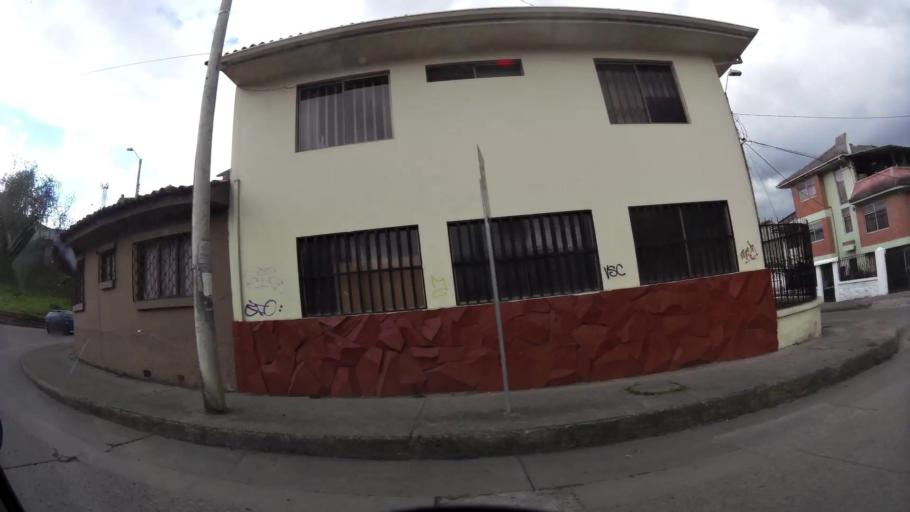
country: EC
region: Azuay
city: Cuenca
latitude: -2.8950
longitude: -79.0149
